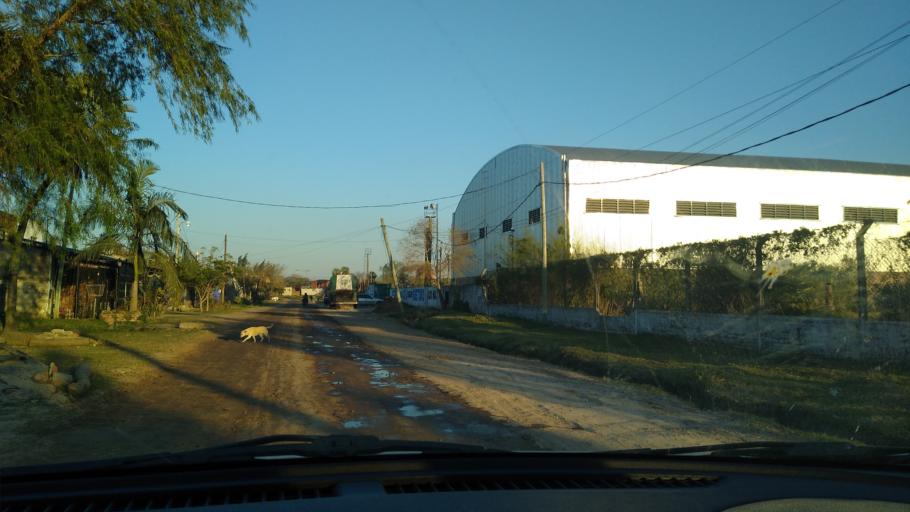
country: AR
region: Chaco
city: Puerto Vilelas
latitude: -27.5126
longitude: -58.9440
